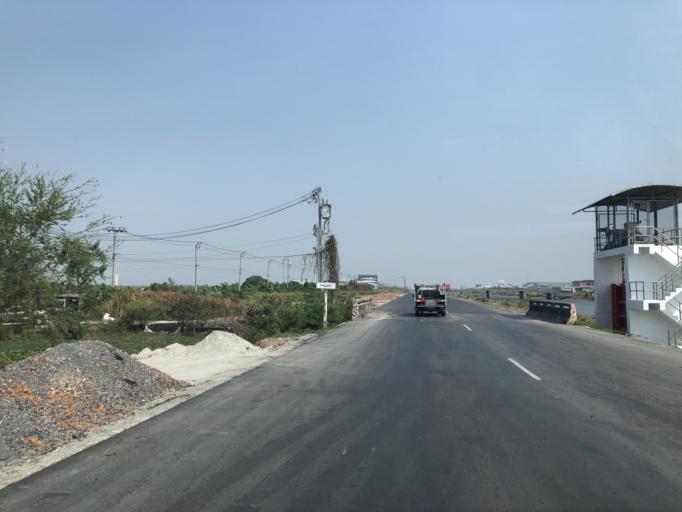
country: TH
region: Samut Prakan
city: Bang Bo District
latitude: 13.5521
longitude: 100.7526
